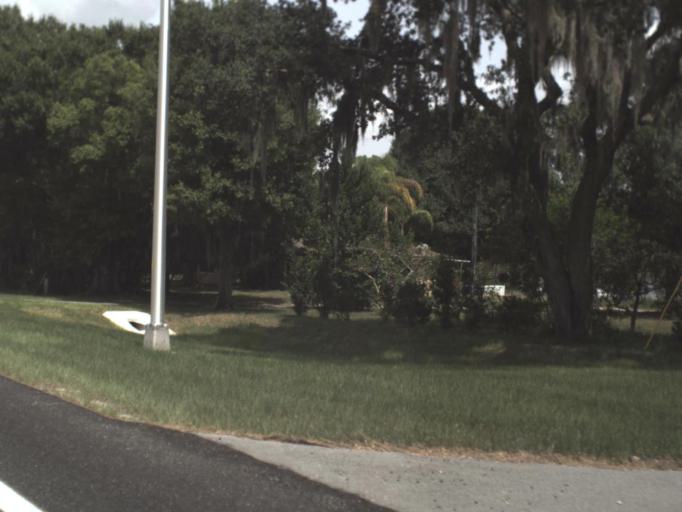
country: US
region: Florida
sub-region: Highlands County
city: Avon Park
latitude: 27.6226
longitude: -81.5144
